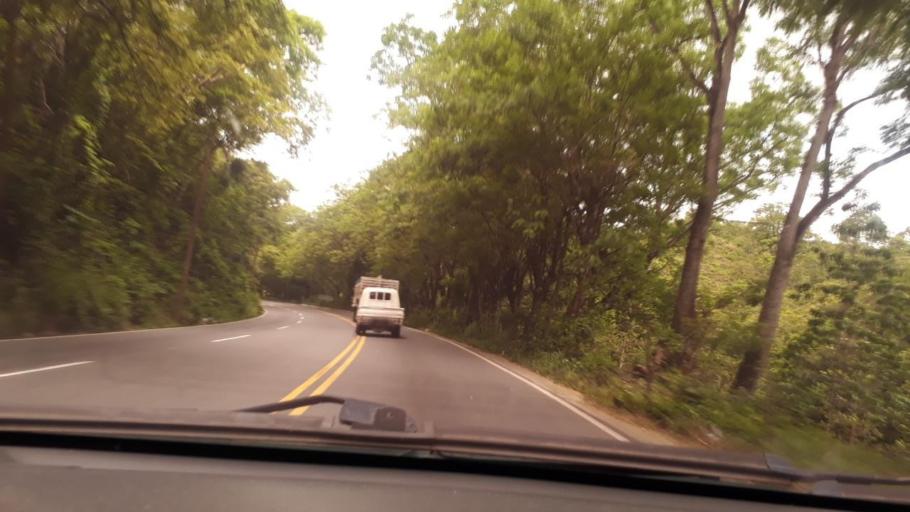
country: GT
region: Izabal
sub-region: Municipio de Los Amates
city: Los Amates
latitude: 15.2325
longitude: -89.2055
